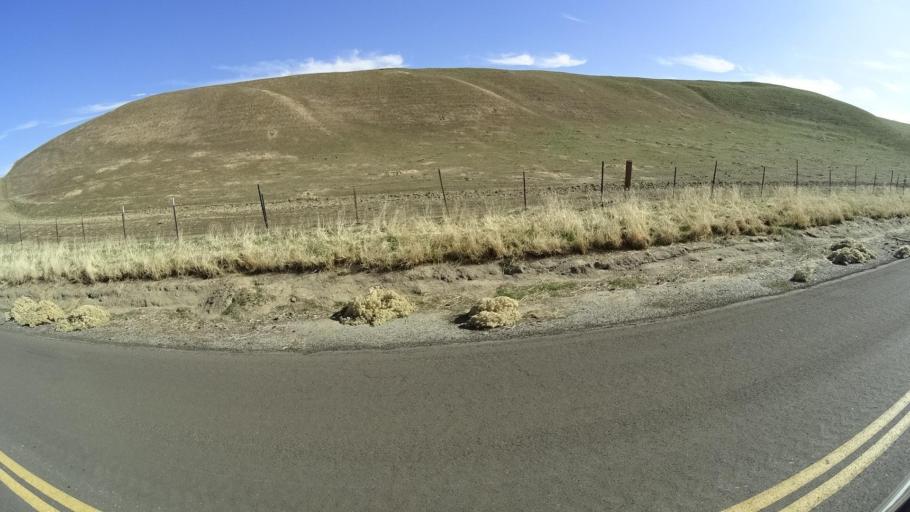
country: US
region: California
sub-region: Tulare County
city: Richgrove
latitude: 35.6505
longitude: -118.9375
